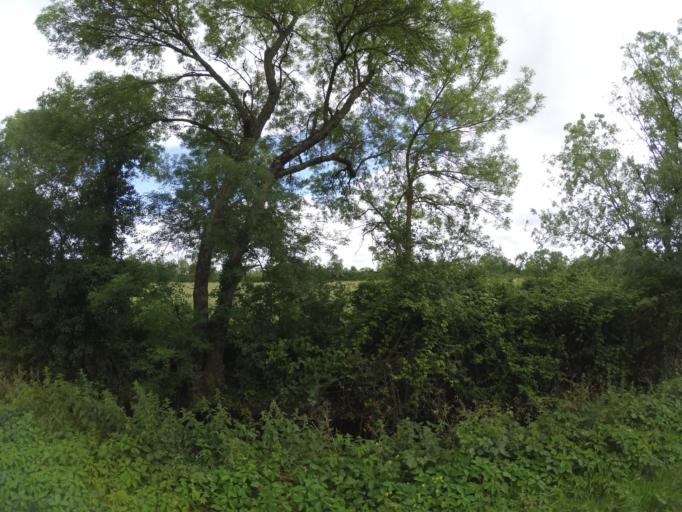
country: FR
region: Aquitaine
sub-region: Departement de la Gironde
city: Ludon-Medoc
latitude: 44.9854
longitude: -0.5759
